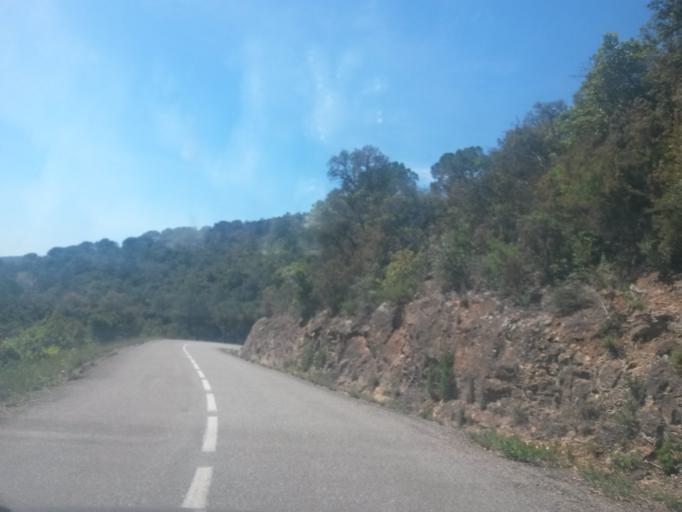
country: ES
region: Catalonia
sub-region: Provincia de Girona
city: Sant Marti Vell
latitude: 41.9833
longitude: 2.9327
